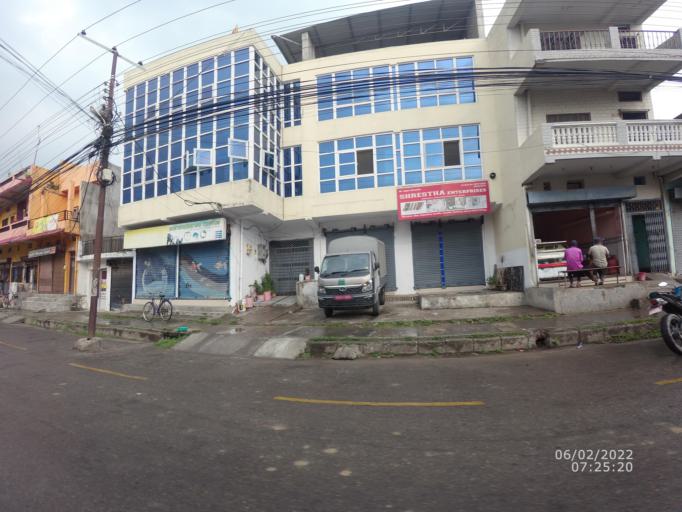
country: NP
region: Western Region
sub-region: Lumbini Zone
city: Bhairahawa
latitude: 27.5016
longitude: 83.4491
